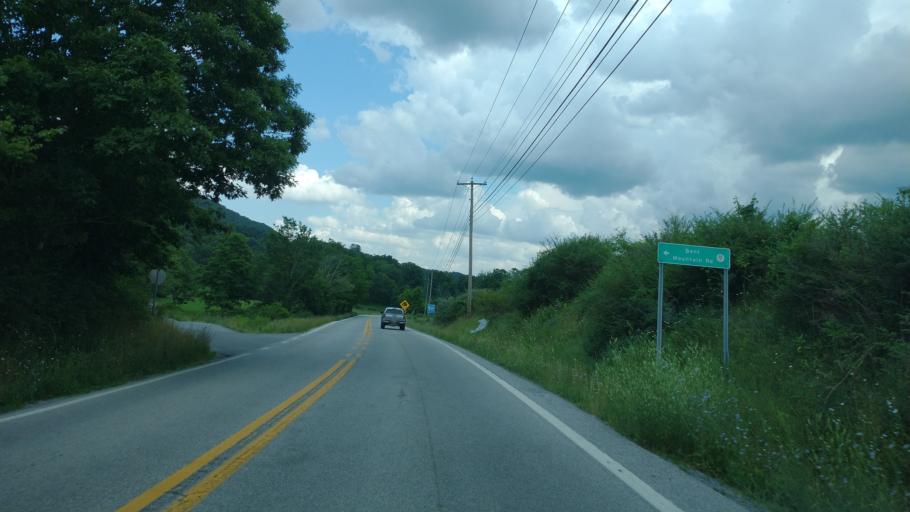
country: US
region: West Virginia
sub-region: Mercer County
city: Athens
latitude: 37.4492
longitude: -81.0052
